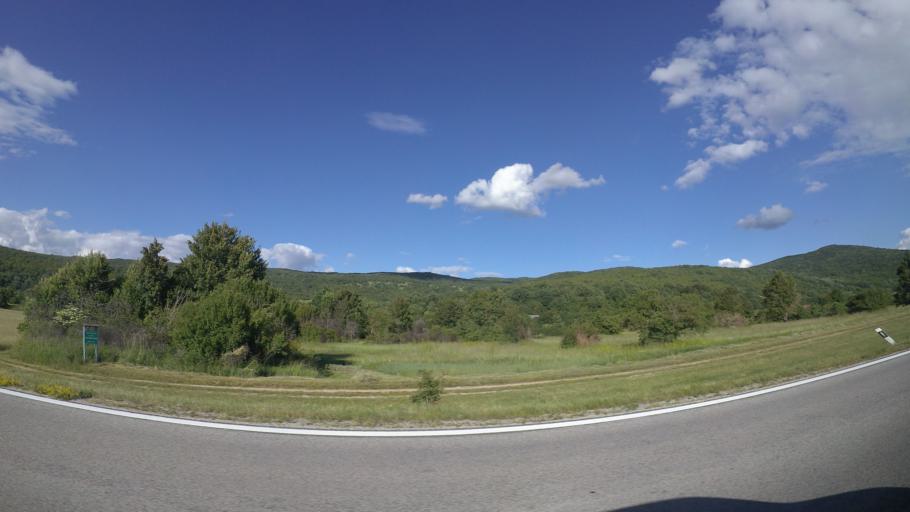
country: BA
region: Federation of Bosnia and Herzegovina
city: Bihac
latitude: 44.6489
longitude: 15.7193
